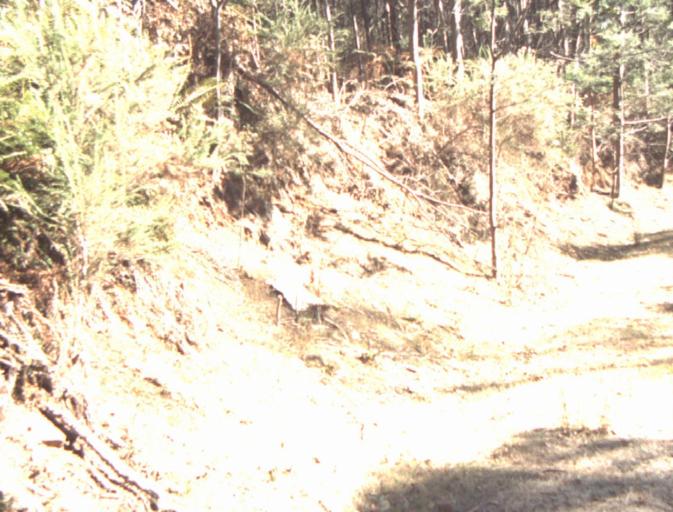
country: AU
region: Tasmania
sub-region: Dorset
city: Scottsdale
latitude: -41.2805
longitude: 147.3583
